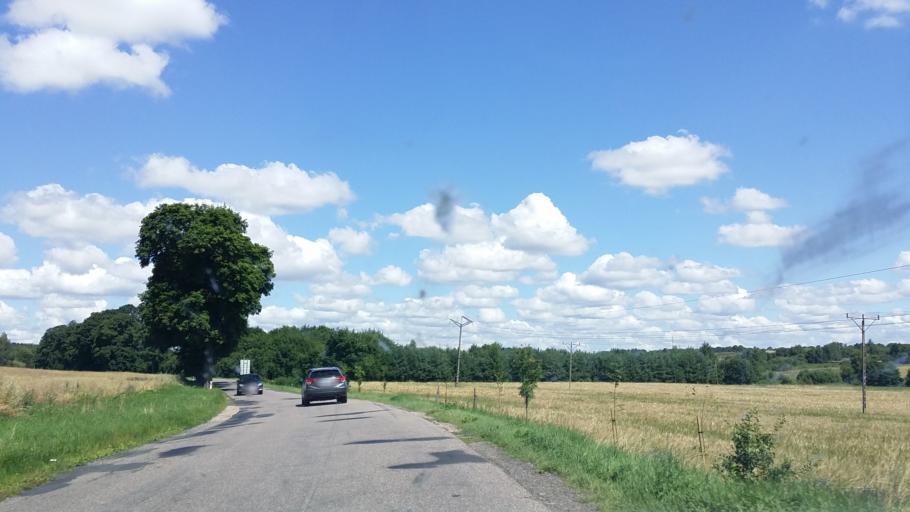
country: PL
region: West Pomeranian Voivodeship
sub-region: Powiat swidwinski
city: Swidwin
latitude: 53.7467
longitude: 15.7717
